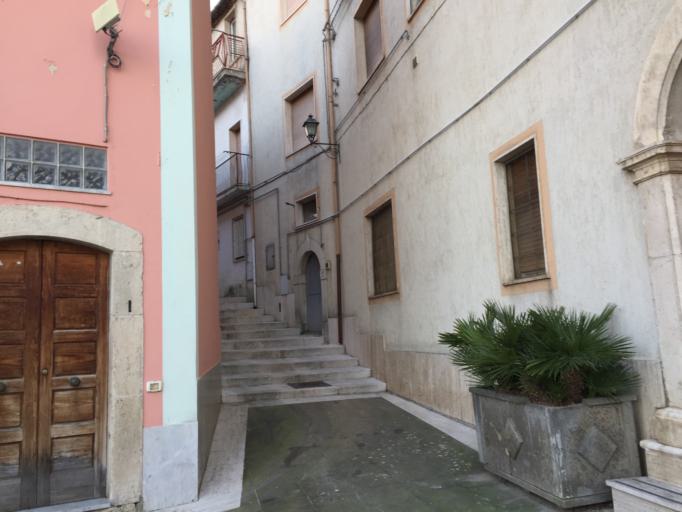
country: IT
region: Molise
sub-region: Provincia di Campobasso
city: Guardiaregia
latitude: 41.4351
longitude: 14.5416
